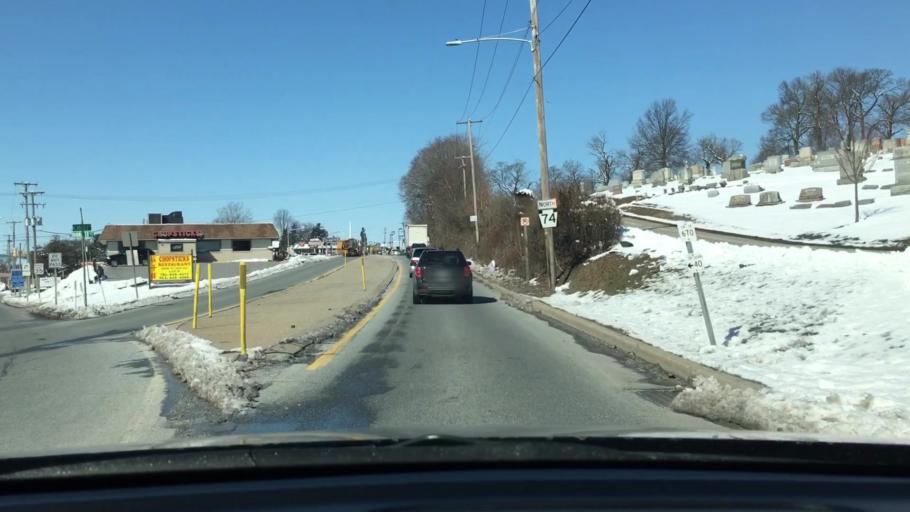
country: US
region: Pennsylvania
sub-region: York County
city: West York
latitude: 39.9611
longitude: -76.7585
